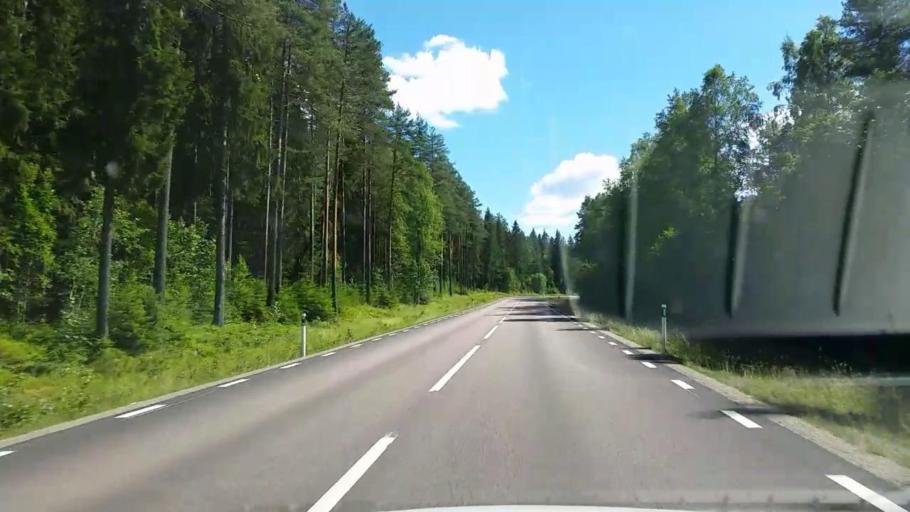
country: SE
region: Dalarna
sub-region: Faluns Kommun
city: Svardsjo
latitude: 60.7751
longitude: 15.7541
